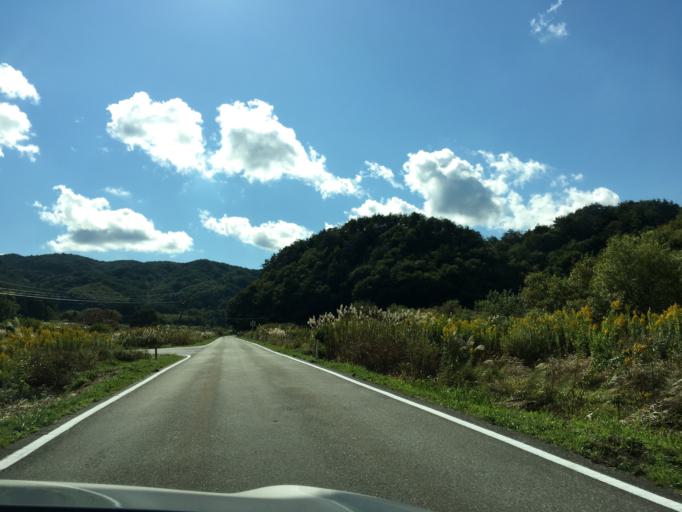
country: JP
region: Fukushima
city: Namie
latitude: 37.5600
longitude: 140.7885
